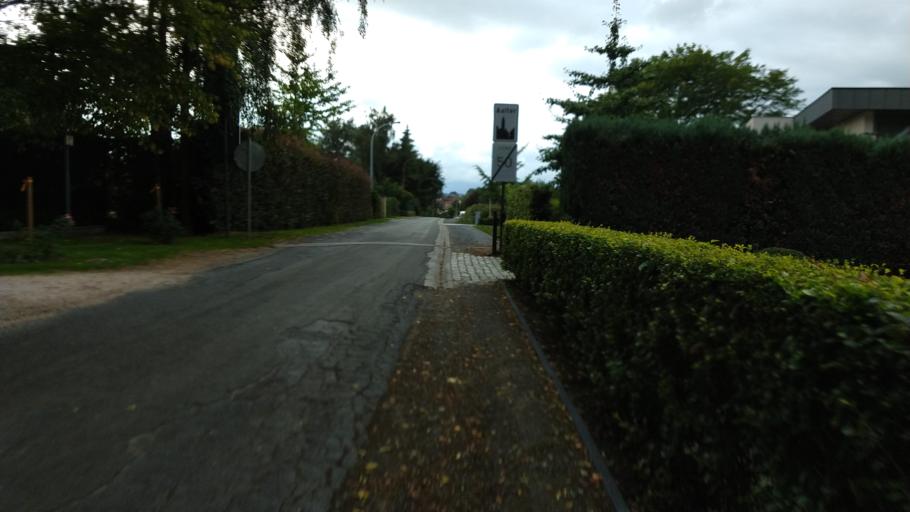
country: BE
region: Flanders
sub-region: Provincie Oost-Vlaanderen
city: Aalter
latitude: 51.0803
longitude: 3.4579
